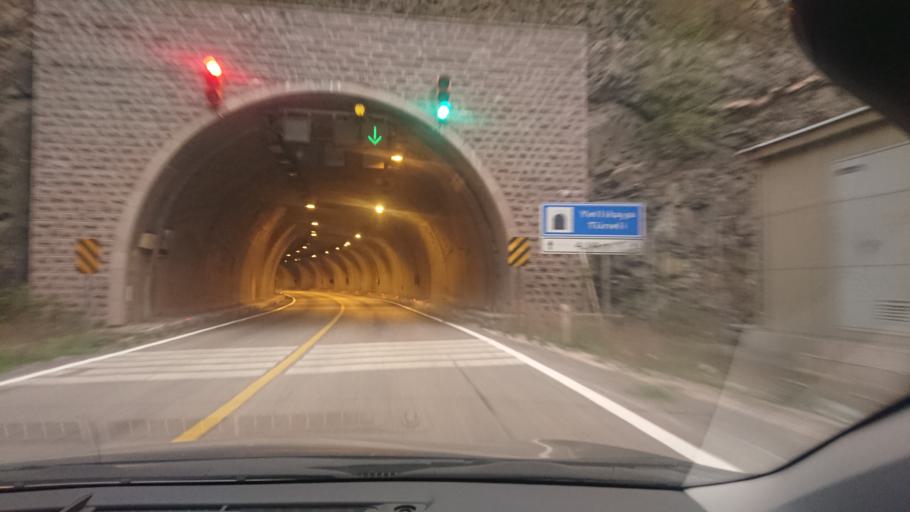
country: TR
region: Karabuk
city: Karabuk
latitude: 41.1639
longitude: 32.4841
